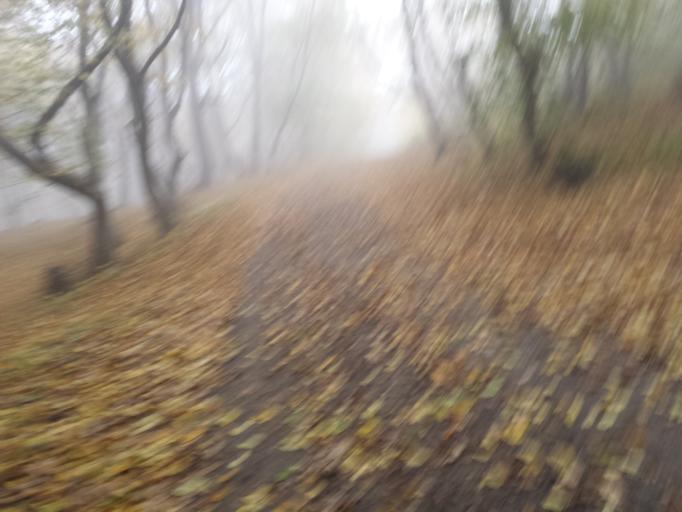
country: RO
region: Cluj
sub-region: Comuna Baciu
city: Baciu
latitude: 46.7748
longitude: 23.5495
